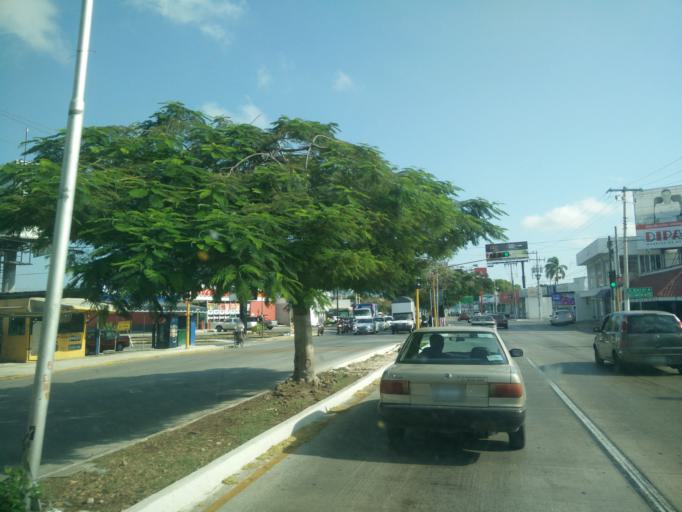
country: MX
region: Yucatan
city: Merida
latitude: 21.0109
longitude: -89.6136
